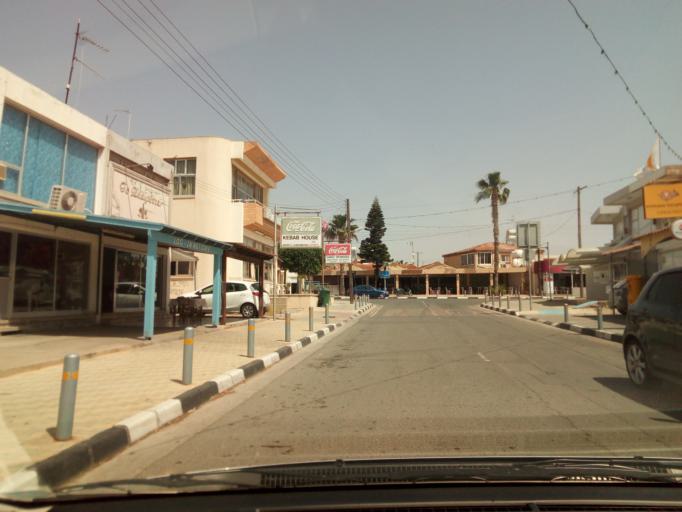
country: CY
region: Larnaka
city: Xylotymbou
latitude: 34.9919
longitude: 33.7790
